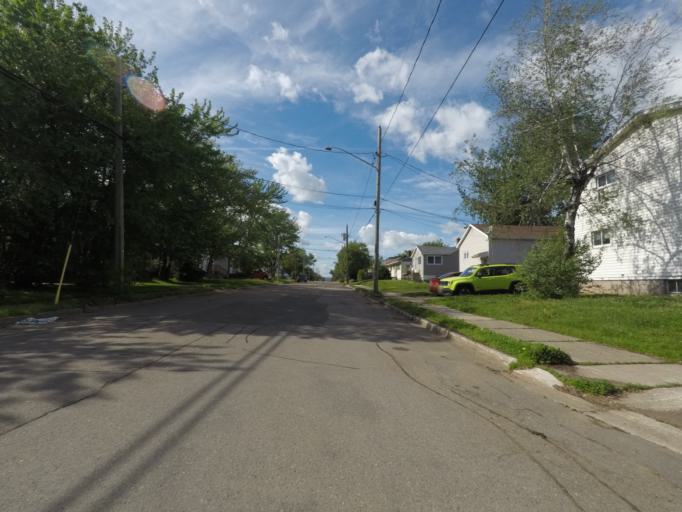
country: CA
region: New Brunswick
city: Moncton
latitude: 46.0999
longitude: -64.8207
